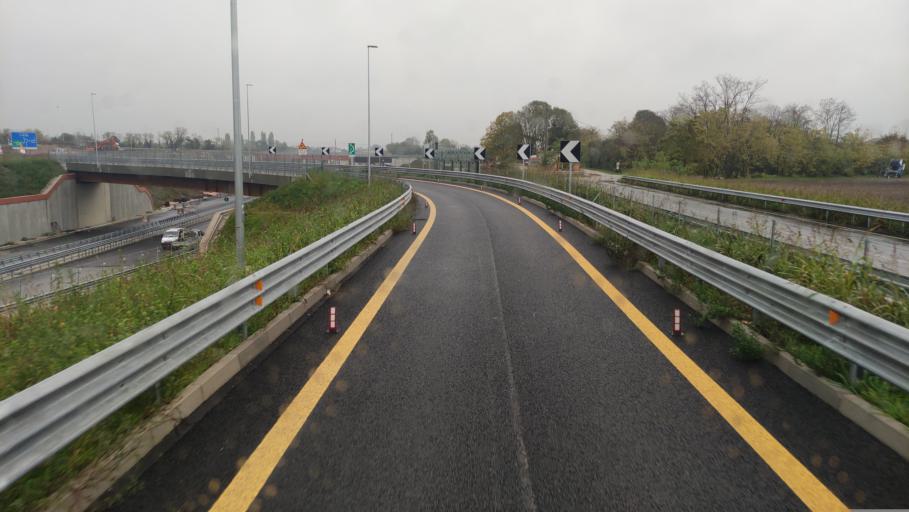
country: IT
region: Veneto
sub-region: Provincia di Treviso
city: Spresiano
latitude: 45.7494
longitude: 12.2628
